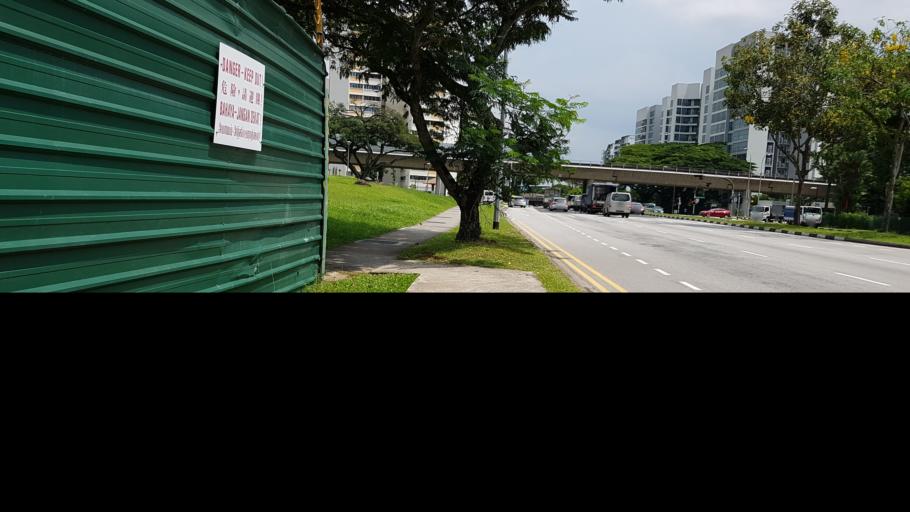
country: MY
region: Johor
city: Kampung Pasir Gudang Baru
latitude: 1.4386
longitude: 103.8340
